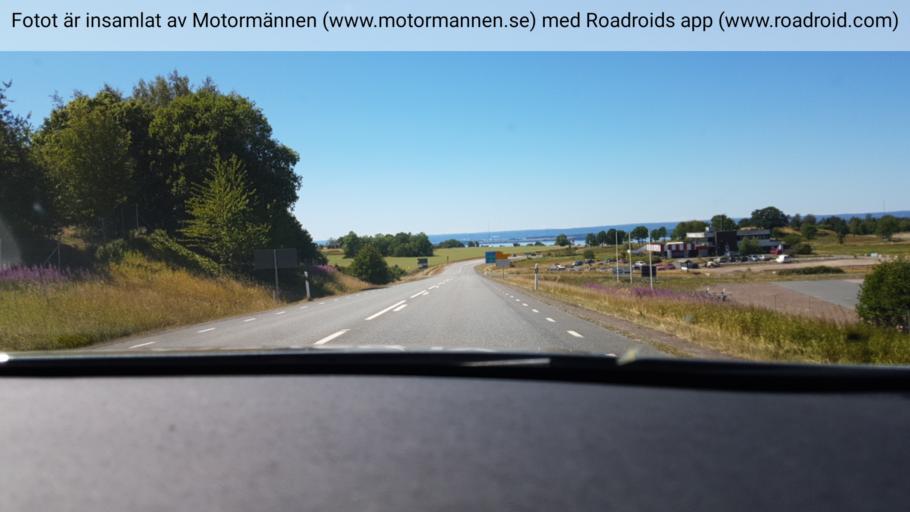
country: SE
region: Joenkoeping
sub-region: Jonkopings Kommun
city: Graenna
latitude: 58.0000
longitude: 14.4631
